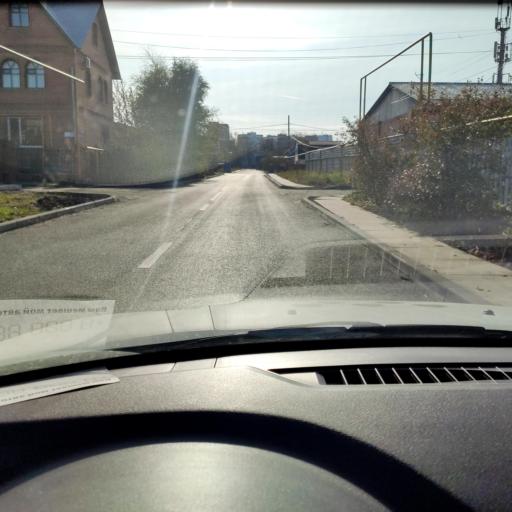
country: RU
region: Samara
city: Tol'yatti
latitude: 53.5276
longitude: 49.4195
